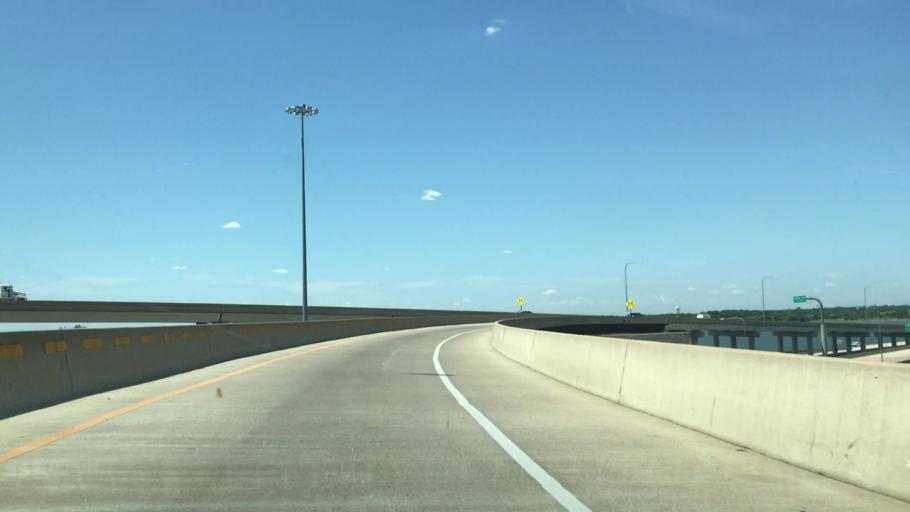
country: US
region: Texas
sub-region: Dallas County
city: Rowlett
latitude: 32.8605
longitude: -96.5541
